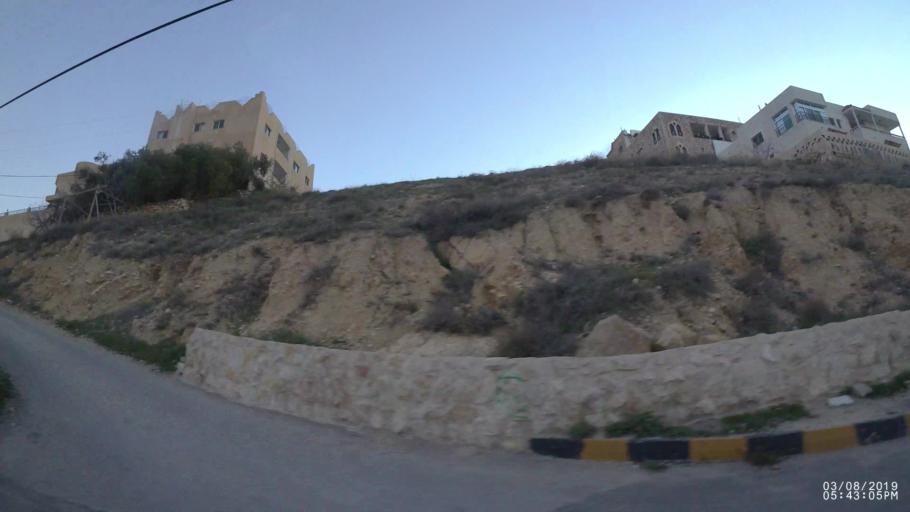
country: JO
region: Ma'an
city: Petra
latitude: 30.3157
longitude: 35.4761
